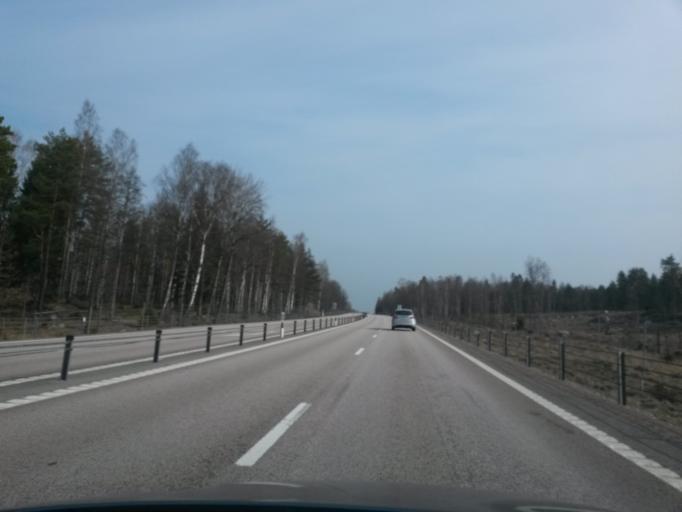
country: SE
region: Vaestra Goetaland
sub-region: Toreboda Kommun
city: Toereboda
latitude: 58.7677
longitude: 13.9863
